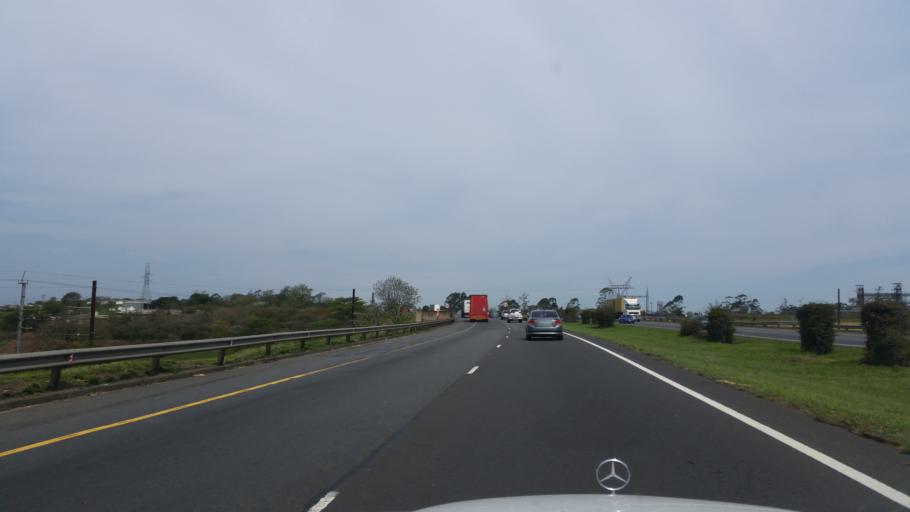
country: ZA
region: KwaZulu-Natal
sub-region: uMgungundlovu District Municipality
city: Camperdown
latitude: -29.7239
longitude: 30.5027
